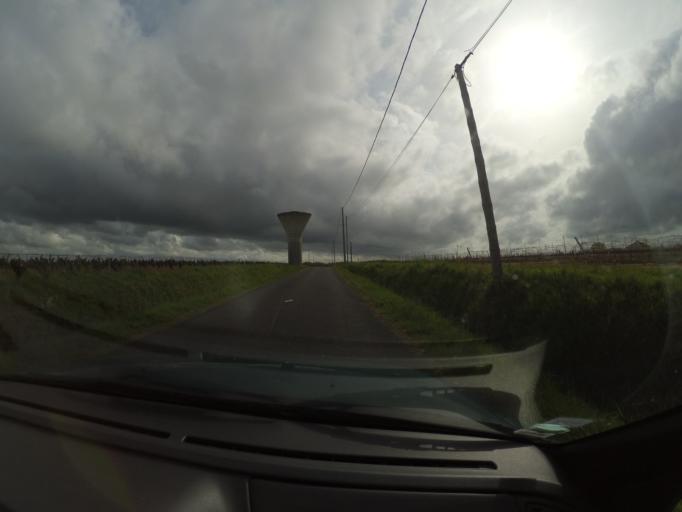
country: FR
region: Pays de la Loire
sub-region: Departement de la Loire-Atlantique
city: Maisdon-sur-Sevre
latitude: 47.1076
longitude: -1.3625
